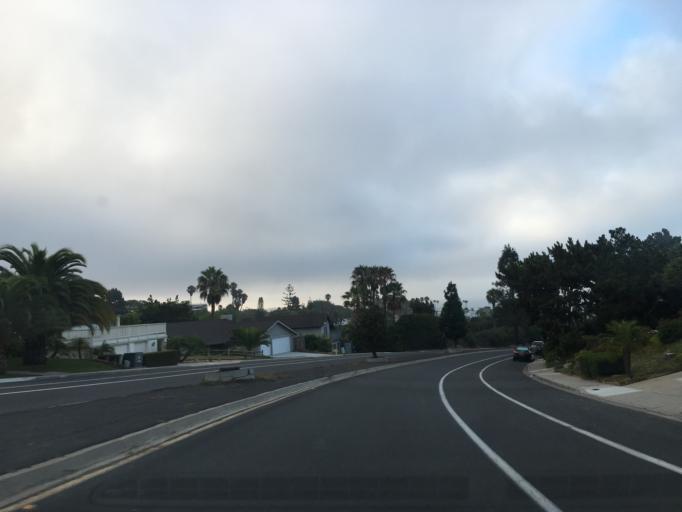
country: US
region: California
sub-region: San Diego County
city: La Jolla
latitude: 32.8148
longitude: -117.2338
